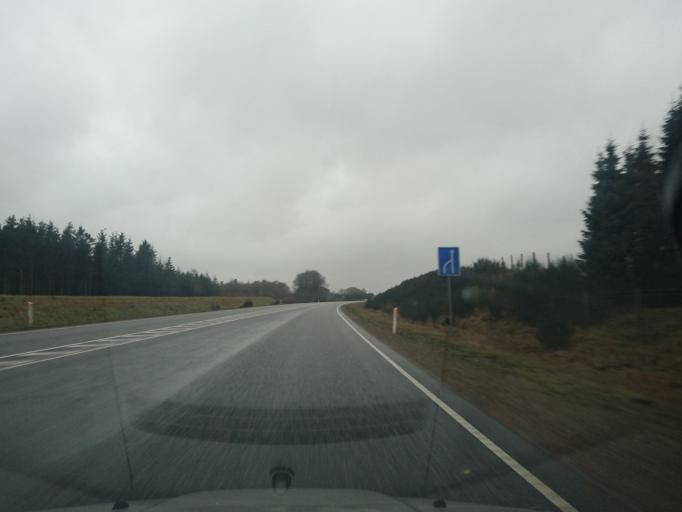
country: DK
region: South Denmark
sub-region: Vejle Kommune
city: Egtved
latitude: 55.7073
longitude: 9.2433
